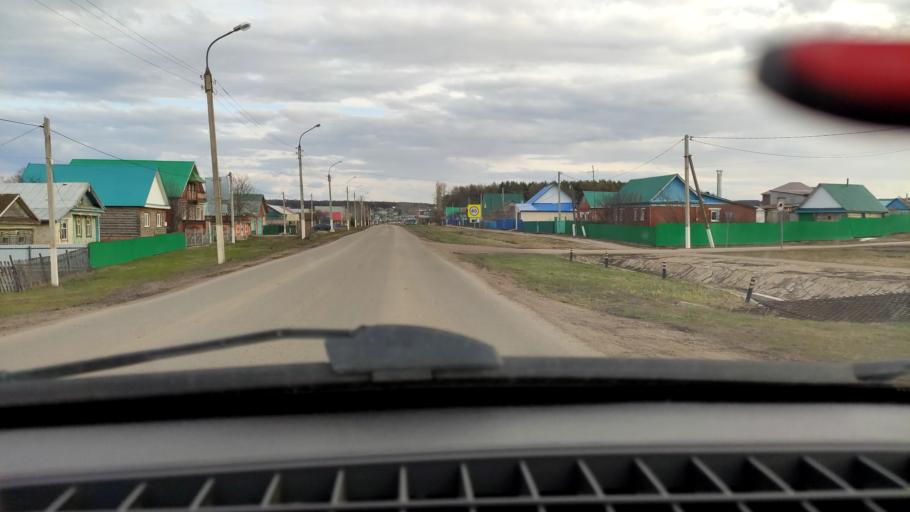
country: RU
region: Bashkortostan
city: Tolbazy
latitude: 54.0289
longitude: 55.8839
